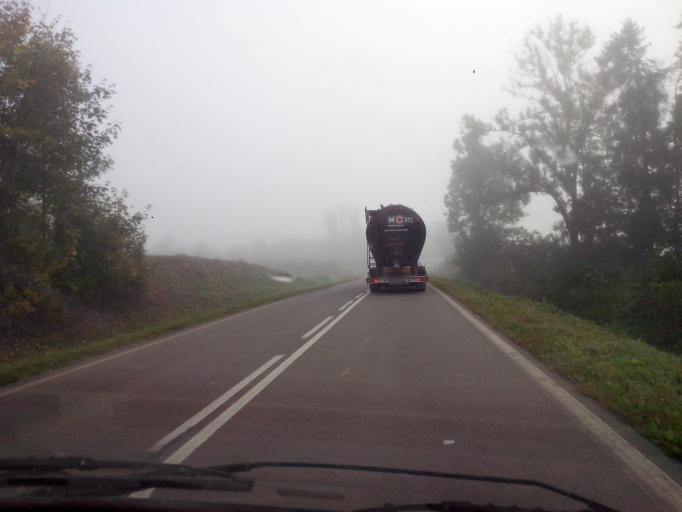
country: PL
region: Subcarpathian Voivodeship
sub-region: Powiat przemyski
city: Krasiczyn
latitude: 49.8056
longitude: 22.6547
